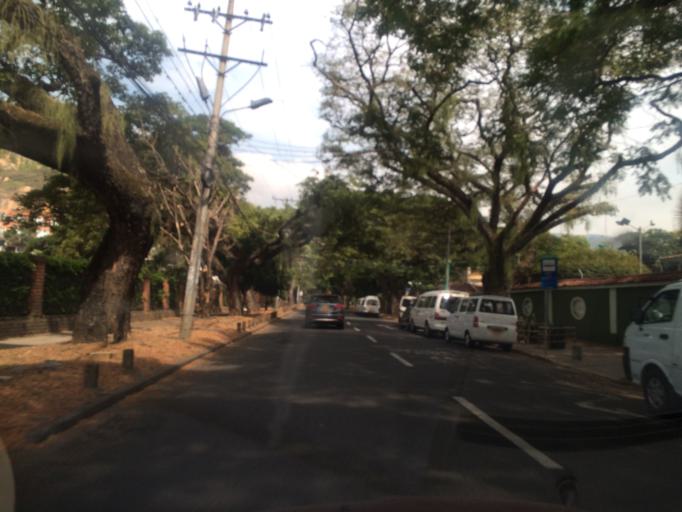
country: CO
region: Valle del Cauca
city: Cali
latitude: 3.4097
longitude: -76.5538
